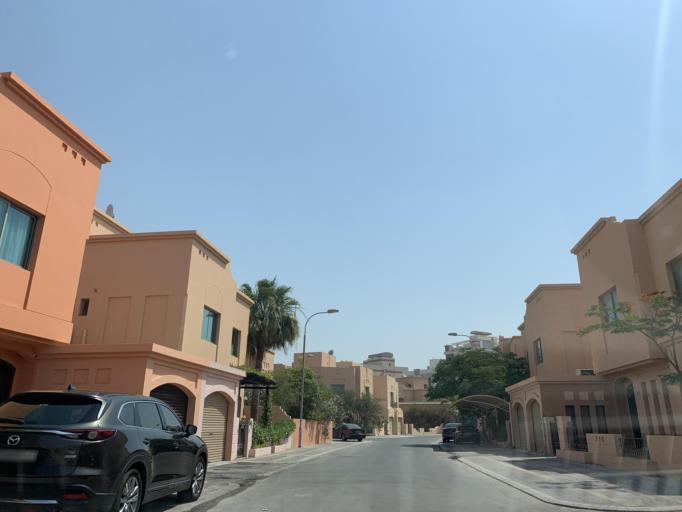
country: BH
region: Manama
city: Jidd Hafs
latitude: 26.2107
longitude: 50.5221
